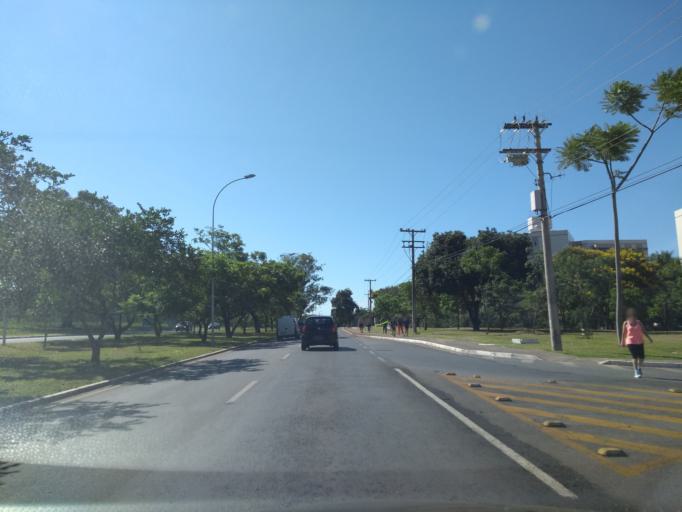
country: BR
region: Federal District
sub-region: Brasilia
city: Brasilia
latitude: -15.8042
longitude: -47.9392
